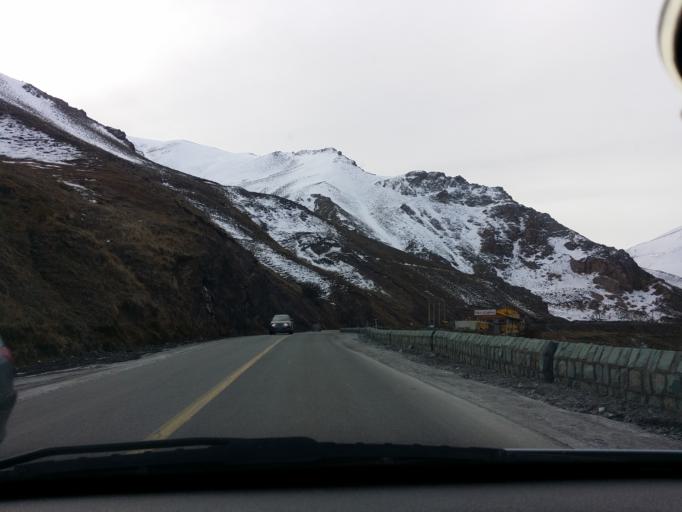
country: IR
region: Tehran
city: Tajrish
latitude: 36.1817
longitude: 51.3185
